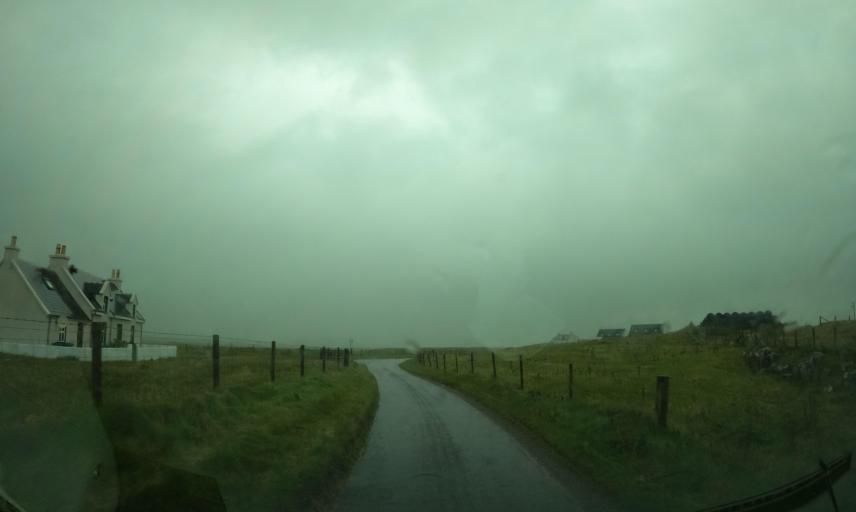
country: GB
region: Scotland
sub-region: Eilean Siar
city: Barra
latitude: 56.4563
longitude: -6.9401
